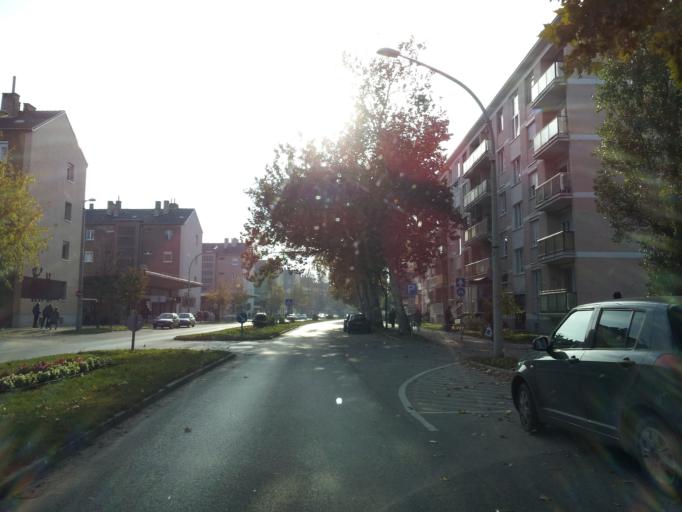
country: HU
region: Komarom-Esztergom
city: Oroszlany
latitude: 47.4871
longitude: 18.3149
